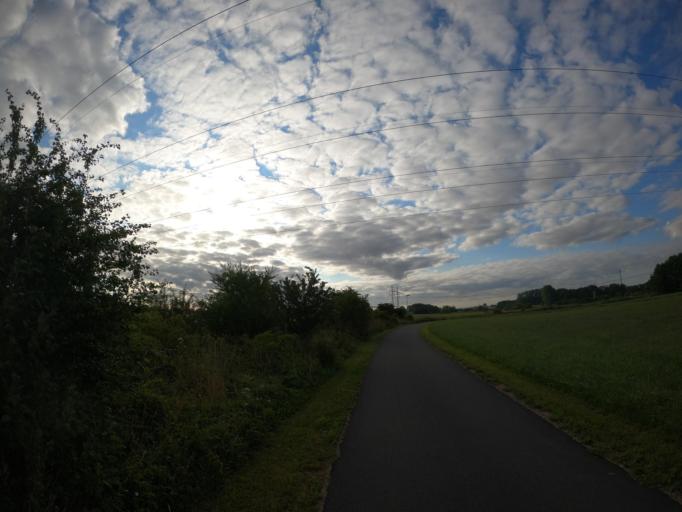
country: SE
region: Skane
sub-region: Staffanstorps Kommun
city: Staffanstorp
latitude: 55.6604
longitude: 13.2110
